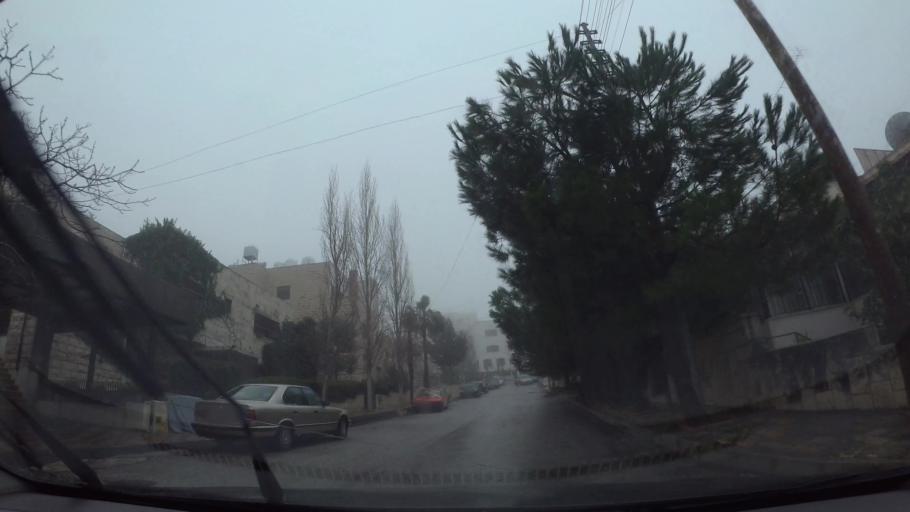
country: JO
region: Amman
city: Al Jubayhah
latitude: 32.0120
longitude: 35.8790
